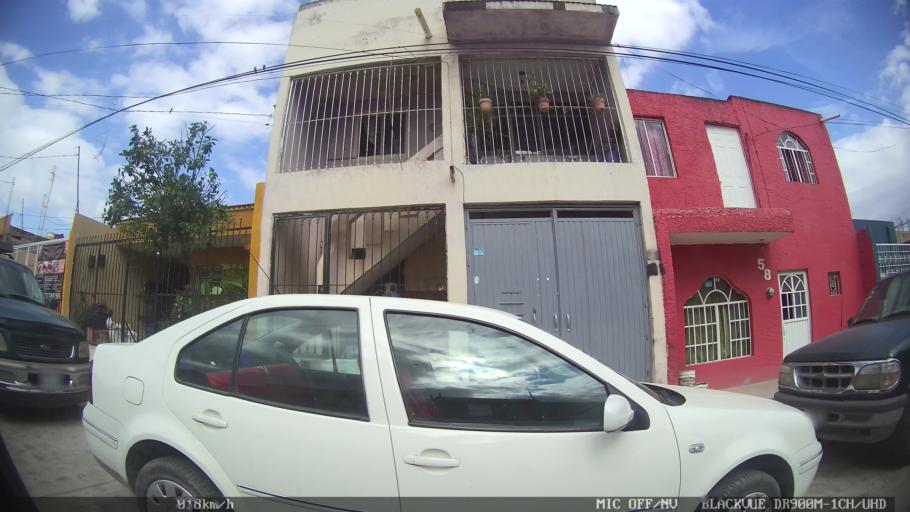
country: MX
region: Jalisco
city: Tlaquepaque
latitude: 20.6759
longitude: -103.2522
